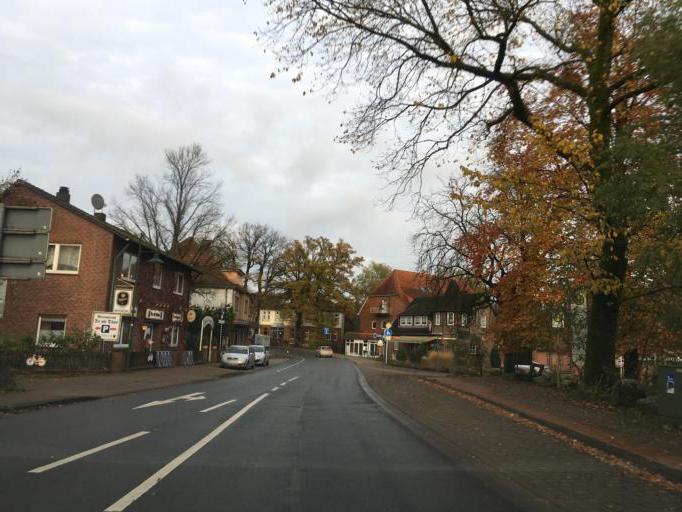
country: DE
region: Lower Saxony
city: Bispingen
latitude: 53.0821
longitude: 9.9965
